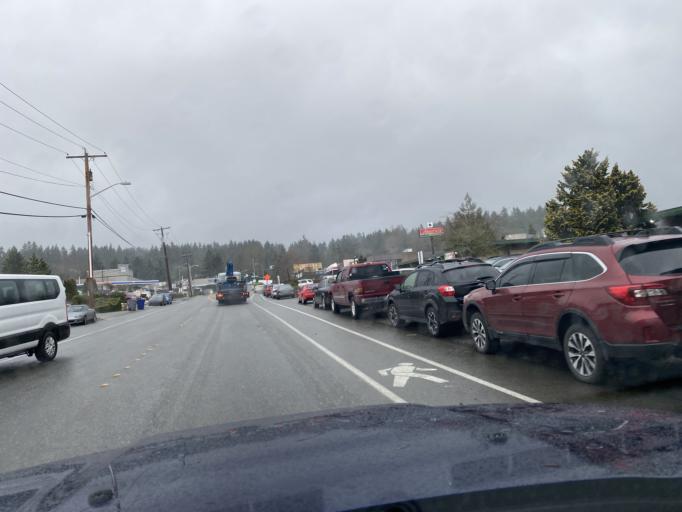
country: US
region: Washington
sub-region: King County
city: Bellevue
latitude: 47.6263
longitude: -122.1670
